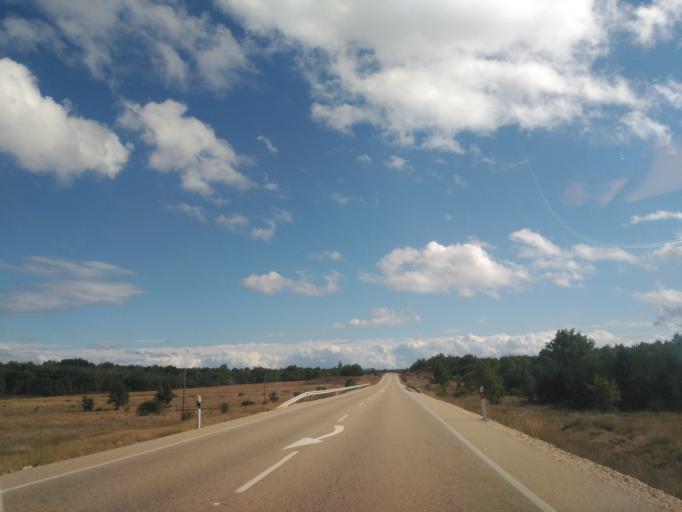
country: ES
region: Castille and Leon
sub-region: Provincia de Burgos
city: Hacinas
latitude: 41.9666
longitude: -3.2944
